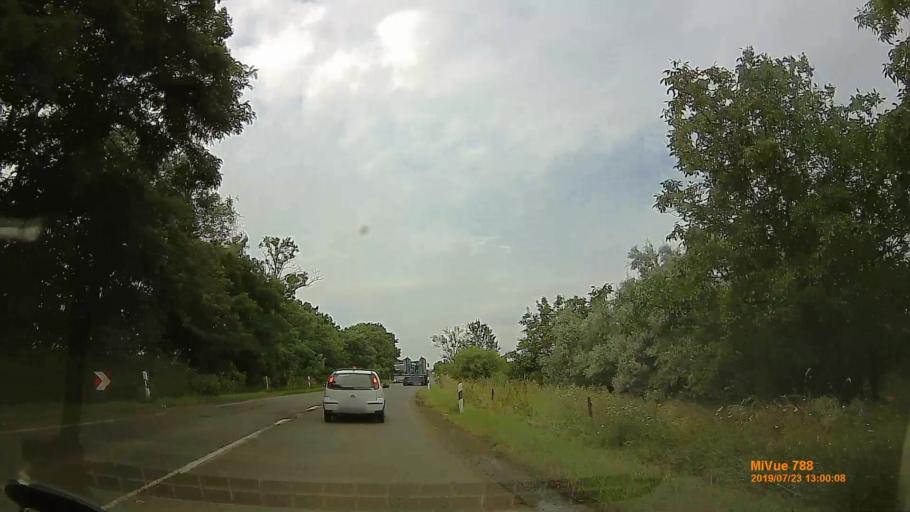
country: HU
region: Szabolcs-Szatmar-Bereg
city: Tiszalok
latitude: 47.9578
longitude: 21.4250
